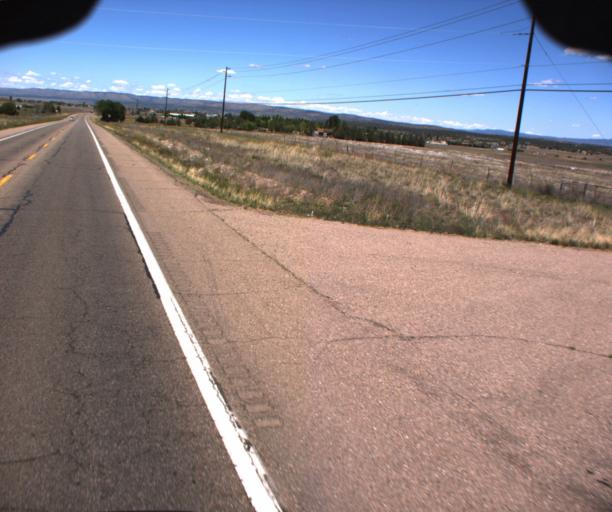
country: US
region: Arizona
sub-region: Yavapai County
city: Paulden
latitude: 34.8376
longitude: -112.4625
